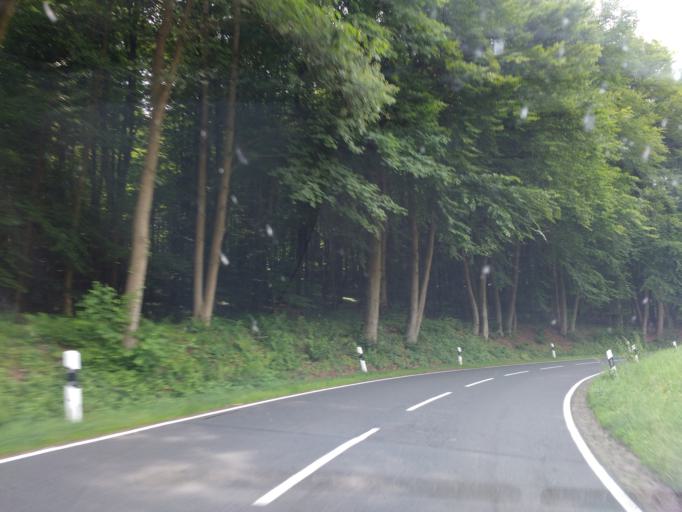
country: DE
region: Lower Saxony
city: Bad Pyrmont
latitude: 51.9954
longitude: 9.2116
